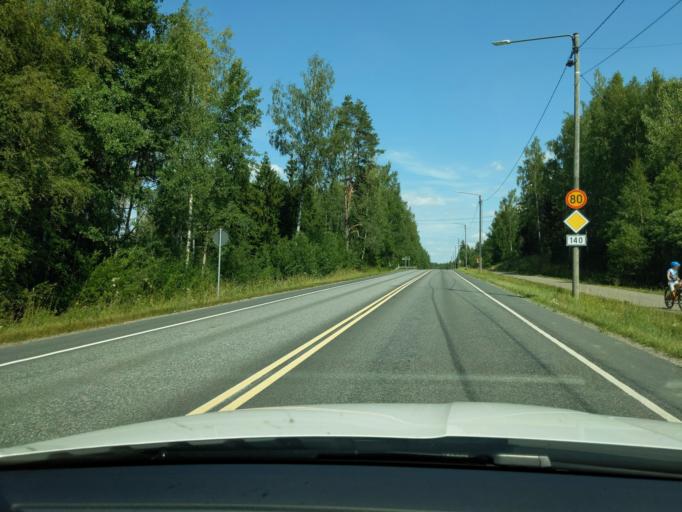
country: FI
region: Uusimaa
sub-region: Helsinki
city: Kerava
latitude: 60.3612
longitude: 25.1283
